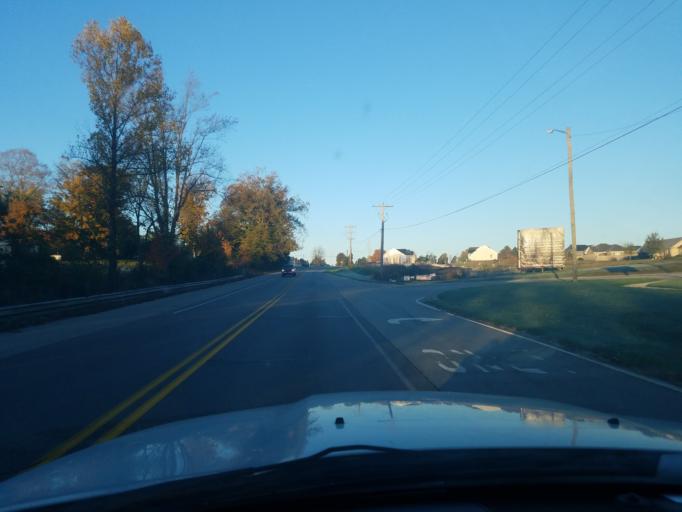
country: US
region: Indiana
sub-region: Floyd County
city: Galena
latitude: 38.3674
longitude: -85.9708
